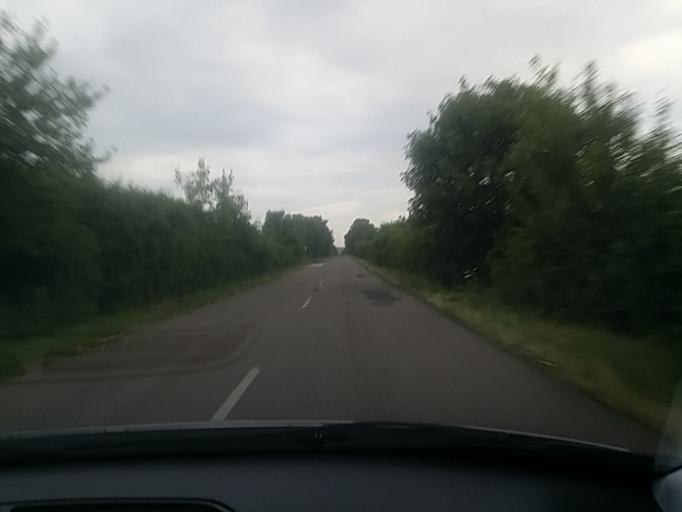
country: HU
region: Nograd
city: Paszto
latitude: 47.9081
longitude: 19.6631
